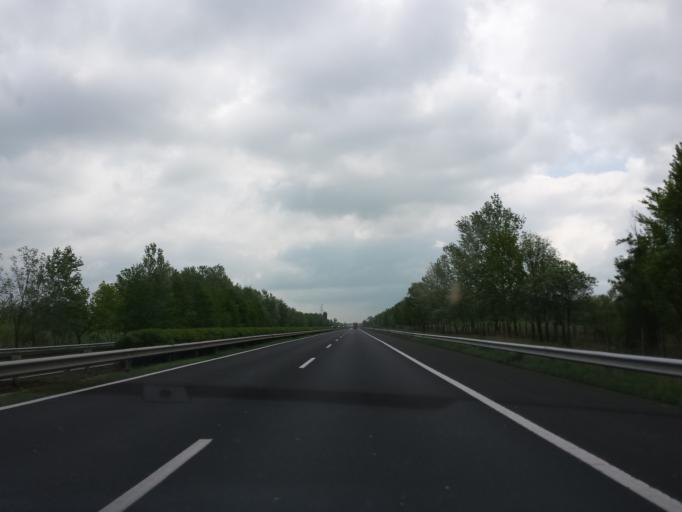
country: HU
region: Gyor-Moson-Sopron
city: Kimle
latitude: 47.7772
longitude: 17.3578
